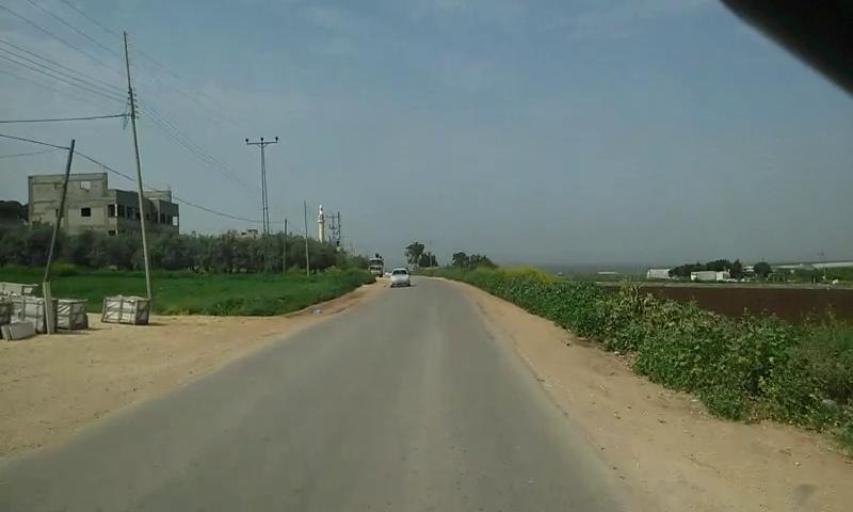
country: PS
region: West Bank
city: Kafr Dan
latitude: 32.4953
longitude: 35.2548
